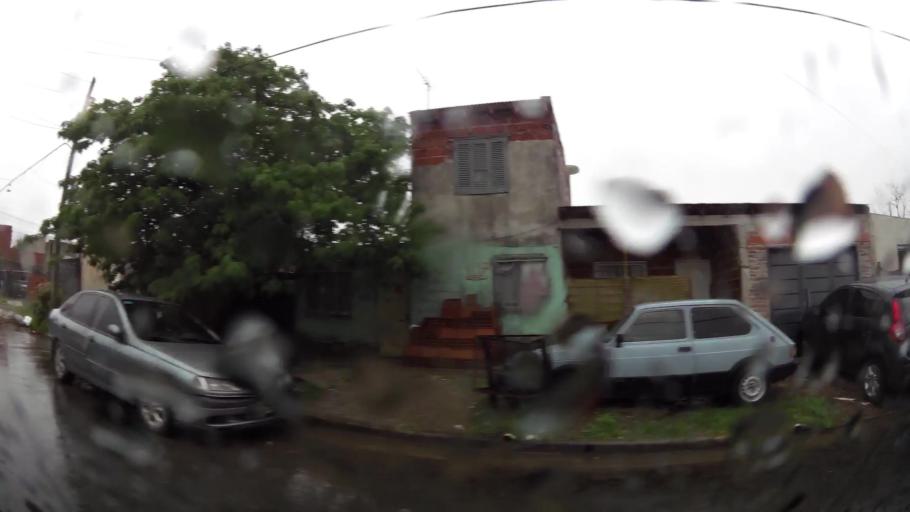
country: AR
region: Buenos Aires
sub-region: Partido de Lanus
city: Lanus
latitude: -34.7207
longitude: -58.4011
